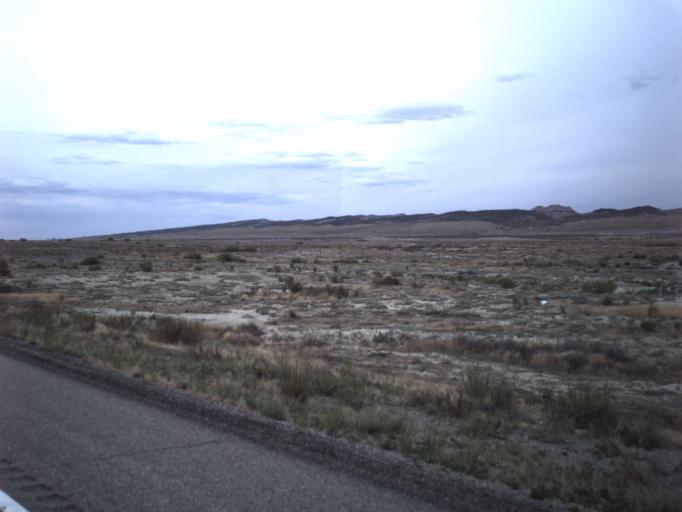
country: US
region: Utah
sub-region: Carbon County
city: East Carbon City
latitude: 39.2278
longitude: -110.3388
